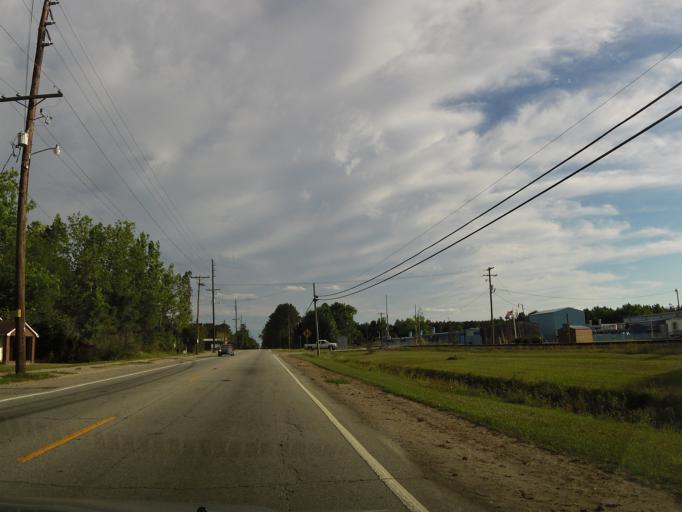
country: US
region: South Carolina
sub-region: Hampton County
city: Estill
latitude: 32.7476
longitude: -81.2415
